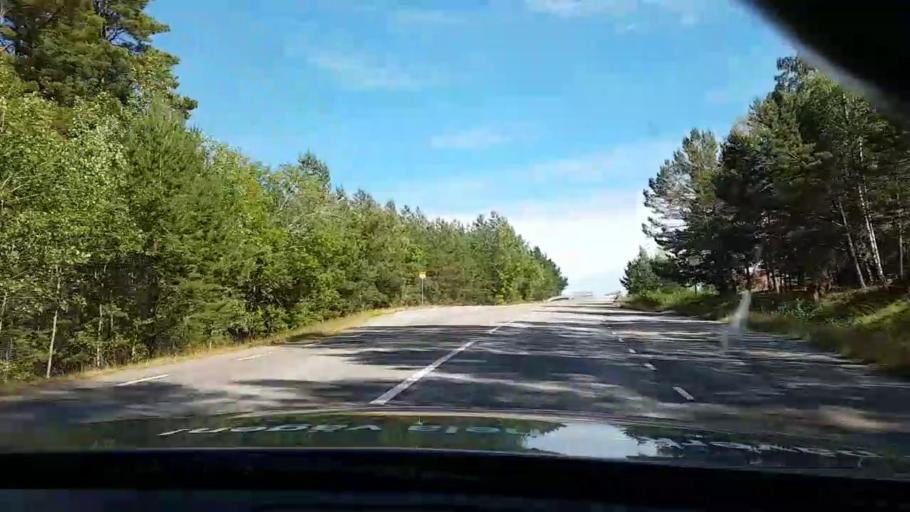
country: SE
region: Kalmar
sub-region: Vasterviks Kommun
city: Forserum
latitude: 57.9212
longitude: 16.5853
